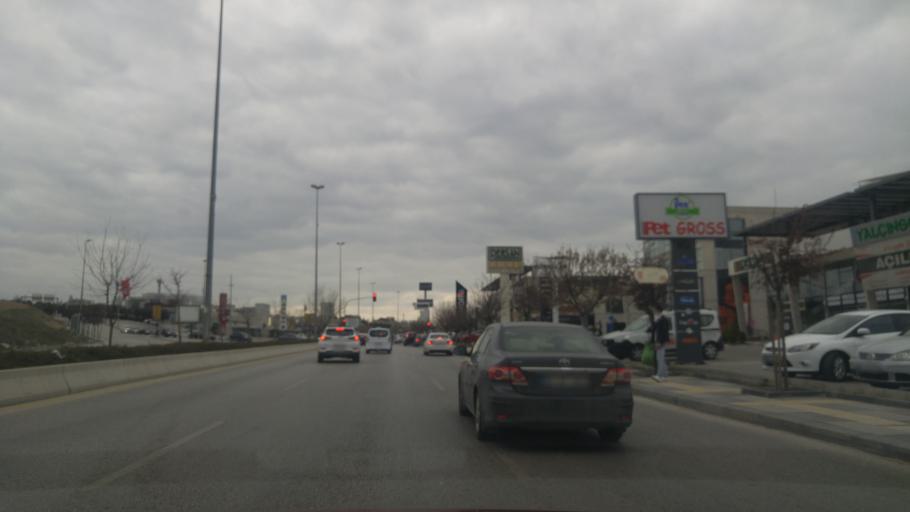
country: TR
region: Ankara
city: Etimesgut
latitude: 39.8687
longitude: 32.6859
